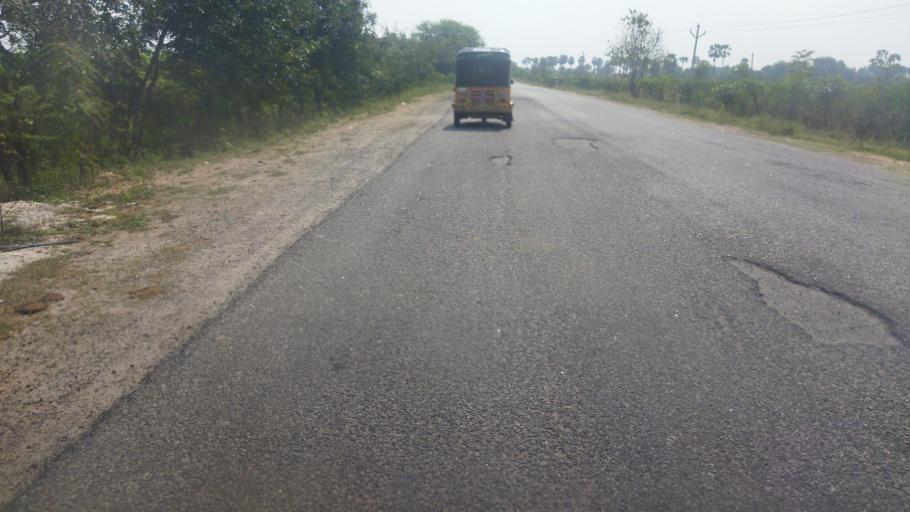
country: IN
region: Telangana
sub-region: Nalgonda
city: Nalgonda
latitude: 17.1079
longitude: 79.2794
